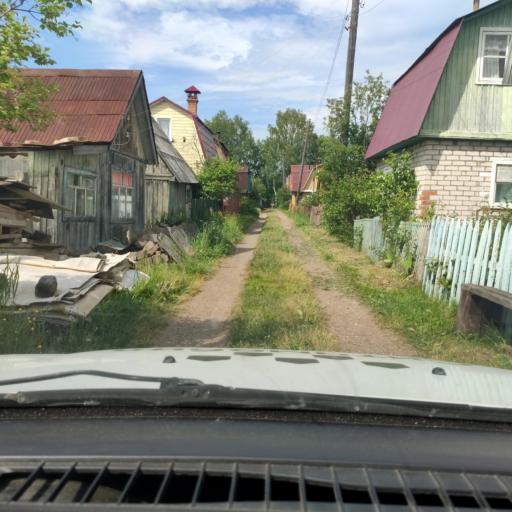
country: RU
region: Perm
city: Overyata
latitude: 58.0540
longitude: 55.9826
